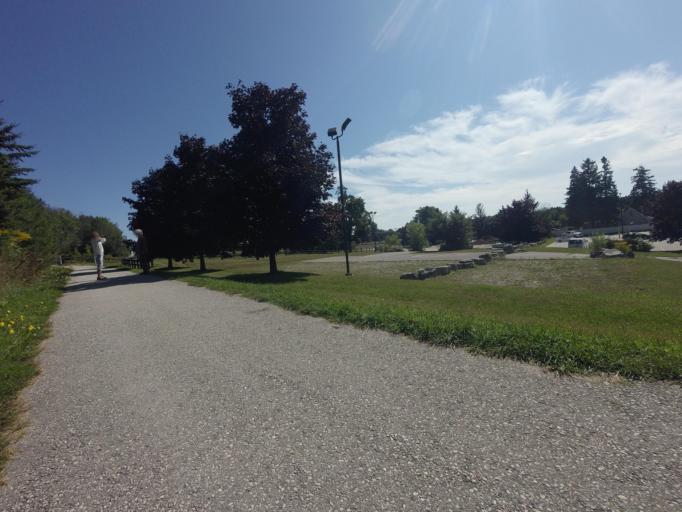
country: CA
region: Ontario
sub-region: Wellington County
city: Guelph
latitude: 43.6925
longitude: -80.4154
